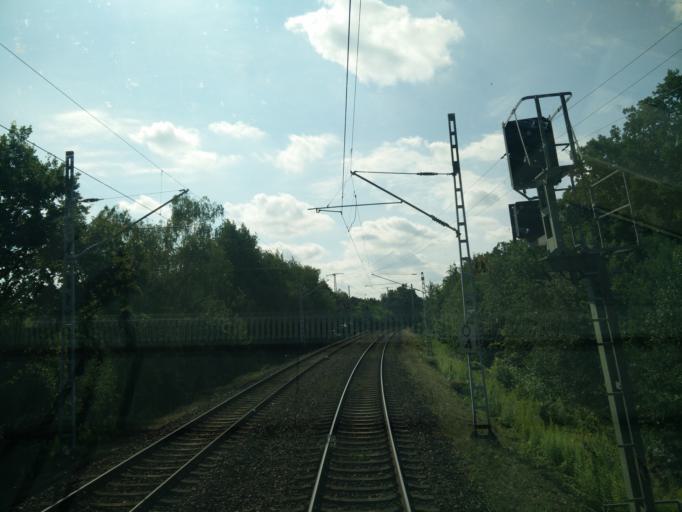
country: DE
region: Berlin
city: Karlshorst
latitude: 52.4692
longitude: 13.5496
